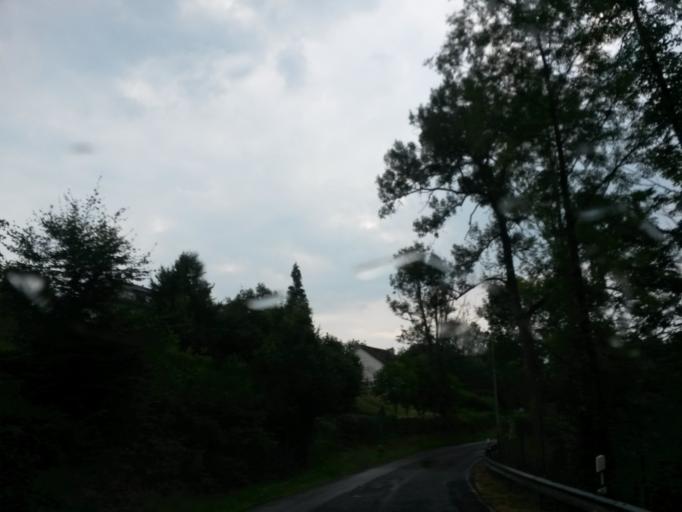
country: DE
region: North Rhine-Westphalia
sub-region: Regierungsbezirk Koln
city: Engelskirchen
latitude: 51.0092
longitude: 7.4668
